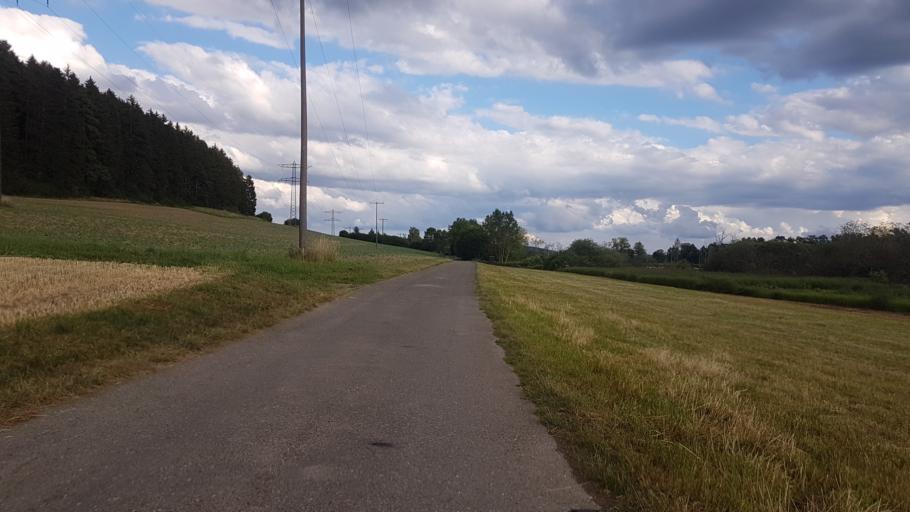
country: DE
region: Baden-Wuerttemberg
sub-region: Freiburg Region
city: Braunlingen
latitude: 47.9874
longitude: 8.4233
